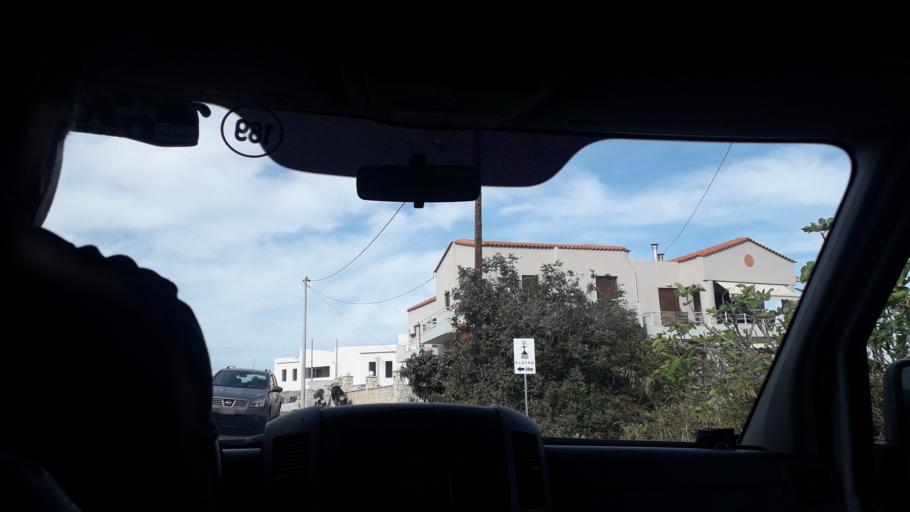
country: GR
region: Crete
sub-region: Nomos Rethymnis
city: Atsipopoulon
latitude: 35.3632
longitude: 24.4366
